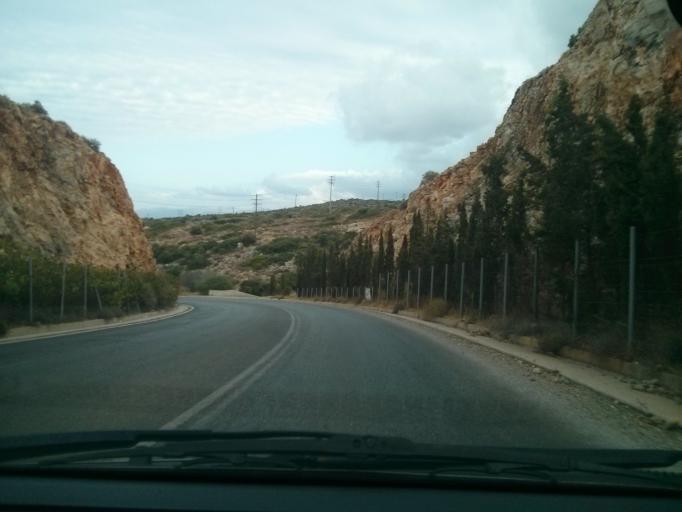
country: GR
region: Crete
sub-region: Nomos Irakleiou
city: Limin Khersonisou
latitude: 35.2988
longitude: 25.4035
